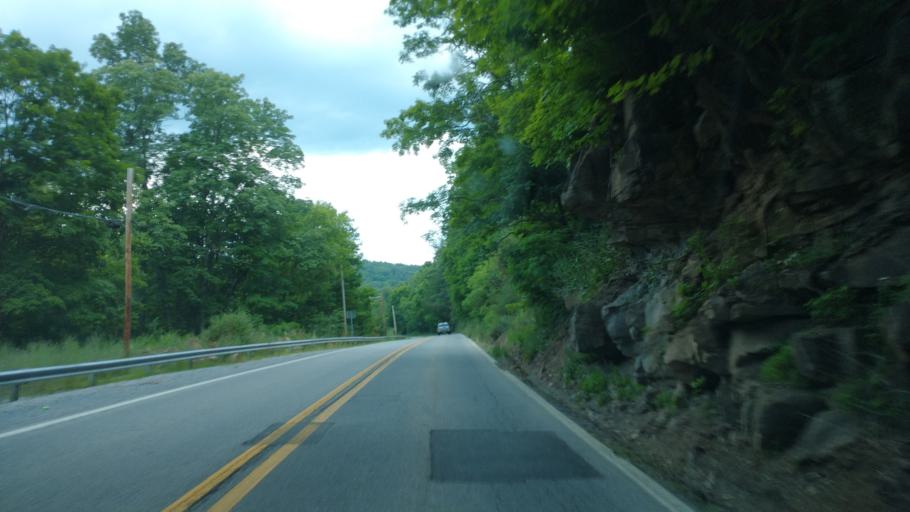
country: US
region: West Virginia
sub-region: Mercer County
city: Athens
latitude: 37.4427
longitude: -81.0018
